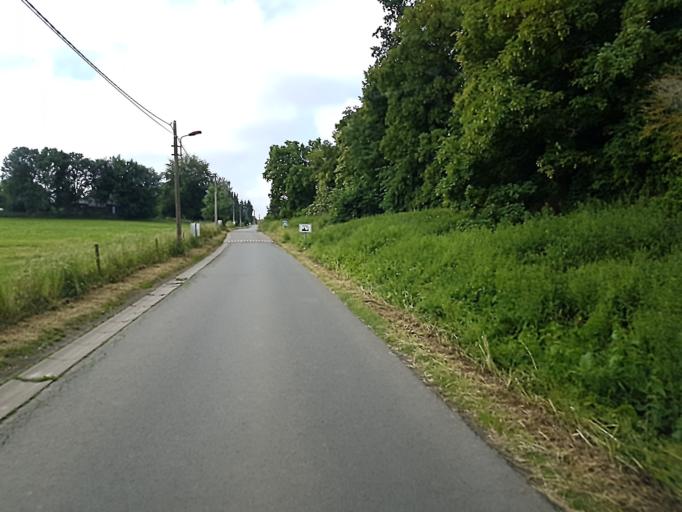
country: BE
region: Wallonia
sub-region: Province du Hainaut
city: Enghien
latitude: 50.6720
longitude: 4.0440
